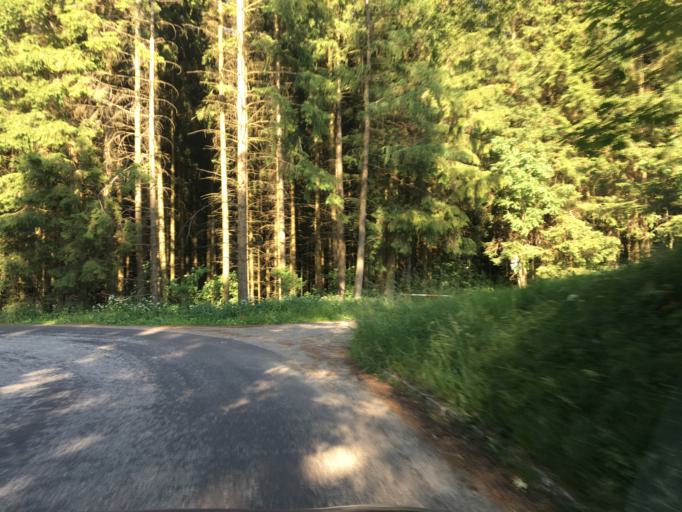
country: AT
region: Upper Austria
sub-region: Politischer Bezirk Urfahr-Umgebung
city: Oberneukirchen
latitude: 48.4687
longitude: 14.2344
